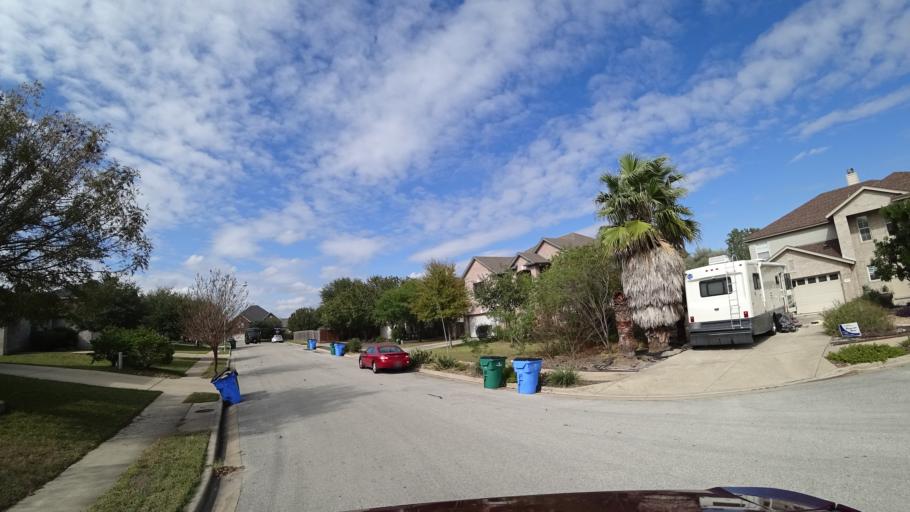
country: US
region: Texas
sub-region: Travis County
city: Pflugerville
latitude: 30.4482
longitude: -97.6257
